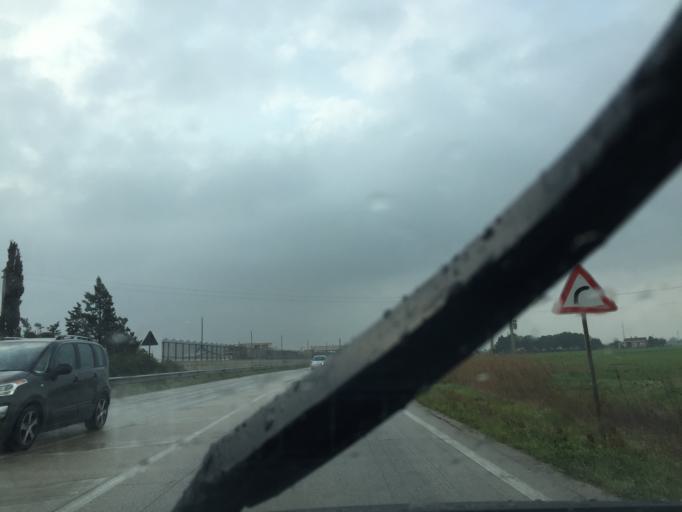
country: IT
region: Apulia
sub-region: Provincia di Foggia
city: Foggia
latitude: 41.4893
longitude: 15.5230
